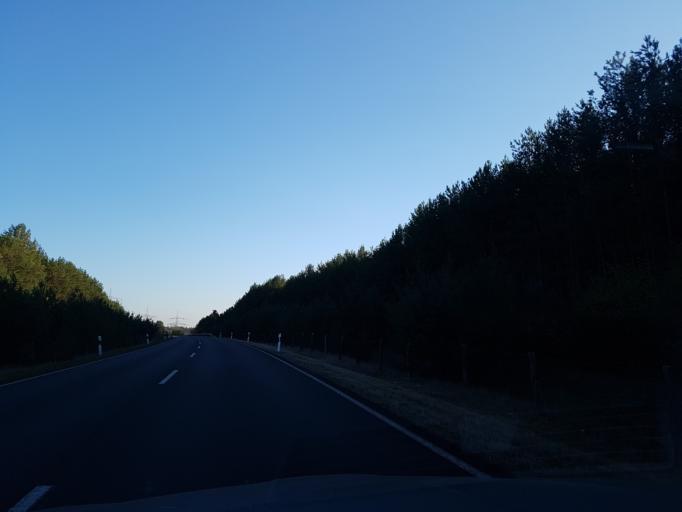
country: DE
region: Brandenburg
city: Bad Liebenwerda
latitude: 51.5230
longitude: 13.4227
